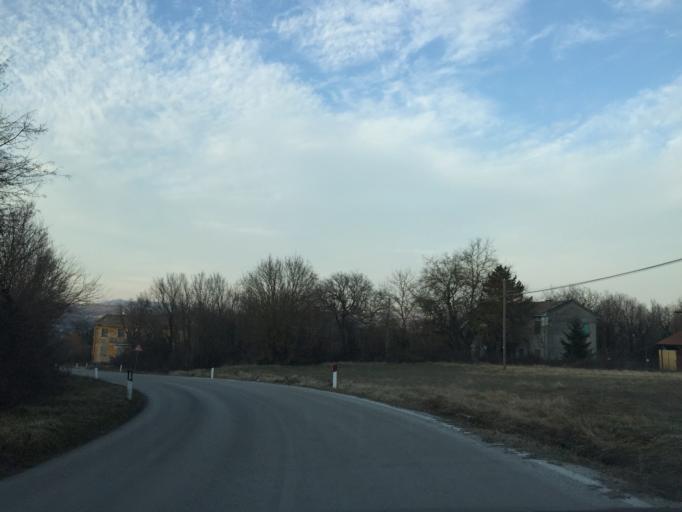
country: IT
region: Molise
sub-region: Provincia di Campobasso
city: Guardiaregia
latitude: 41.4515
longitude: 14.5560
